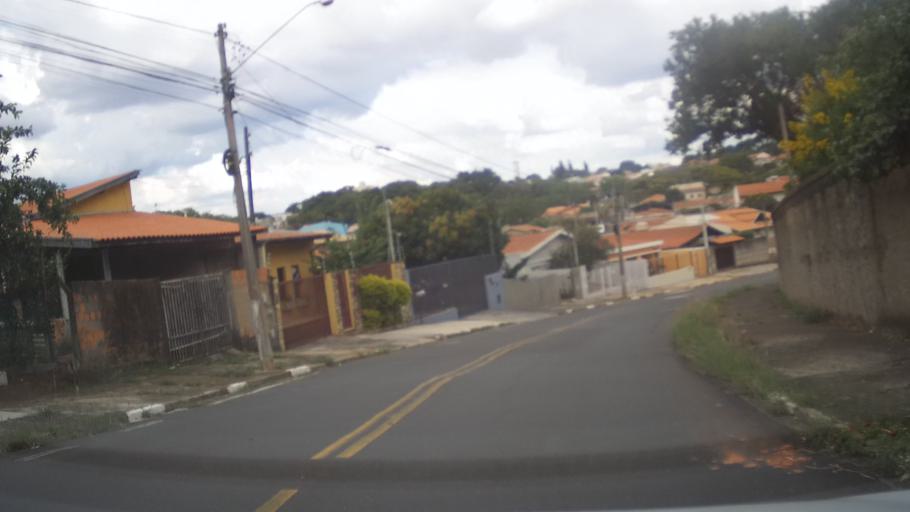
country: BR
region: Sao Paulo
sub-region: Campinas
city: Campinas
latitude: -22.8921
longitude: -47.1080
